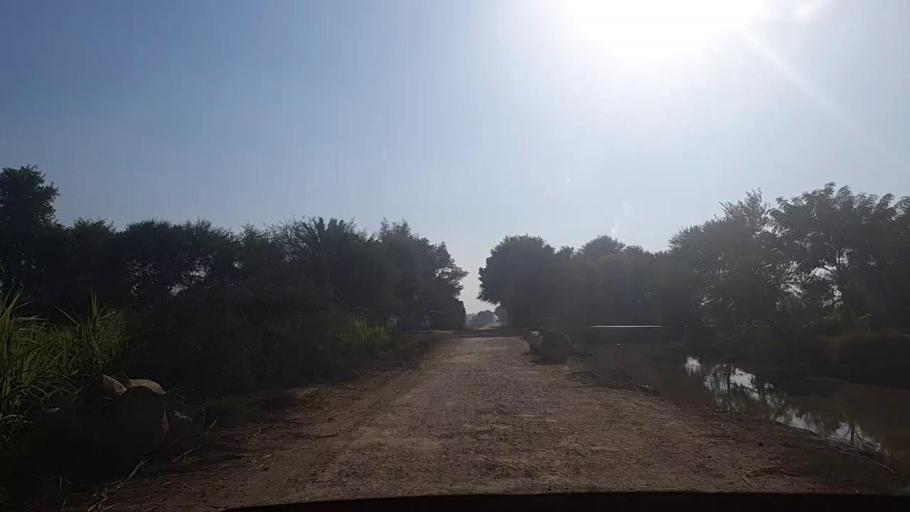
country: PK
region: Sindh
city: Gambat
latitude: 27.3662
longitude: 68.4609
